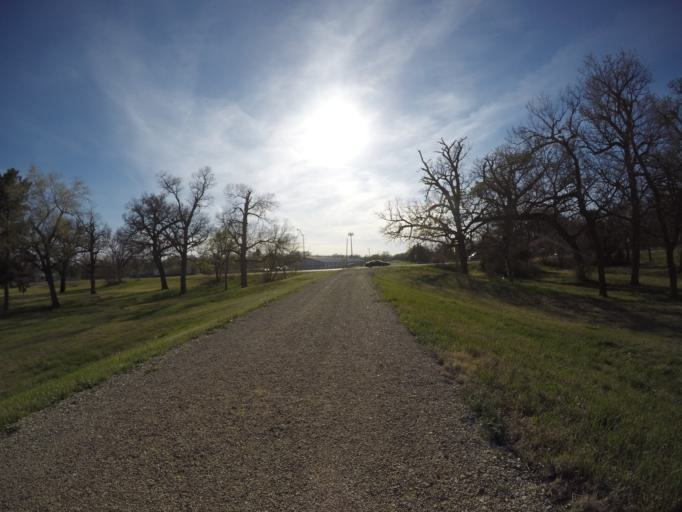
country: US
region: Kansas
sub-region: Saline County
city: Salina
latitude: 38.8649
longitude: -97.6117
